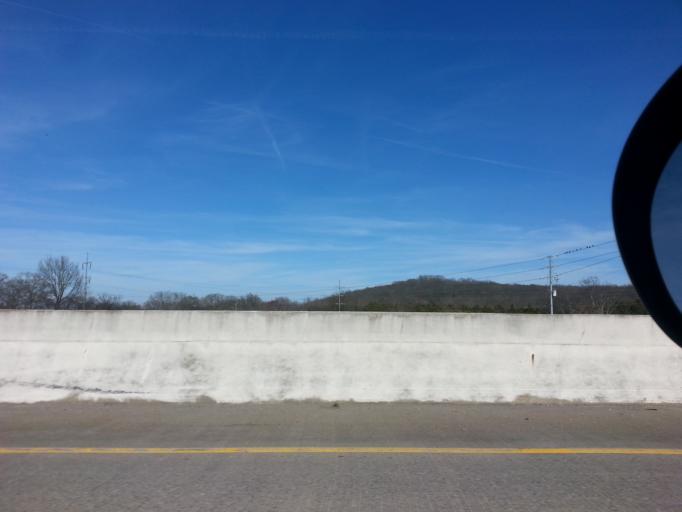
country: US
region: Tennessee
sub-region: Rutherford County
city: Smyrna
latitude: 35.9677
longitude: -86.5665
